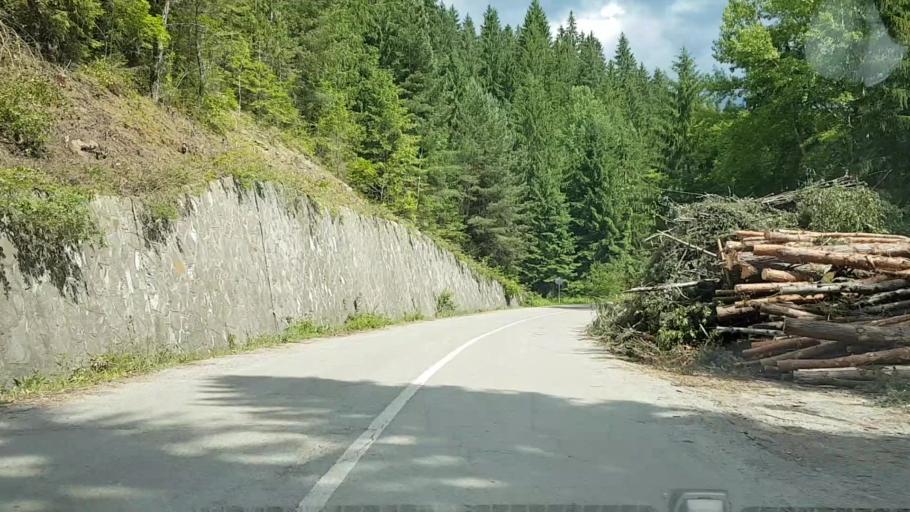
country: RO
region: Neamt
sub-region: Comuna Hangu
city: Hangu
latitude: 47.0528
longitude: 26.0045
